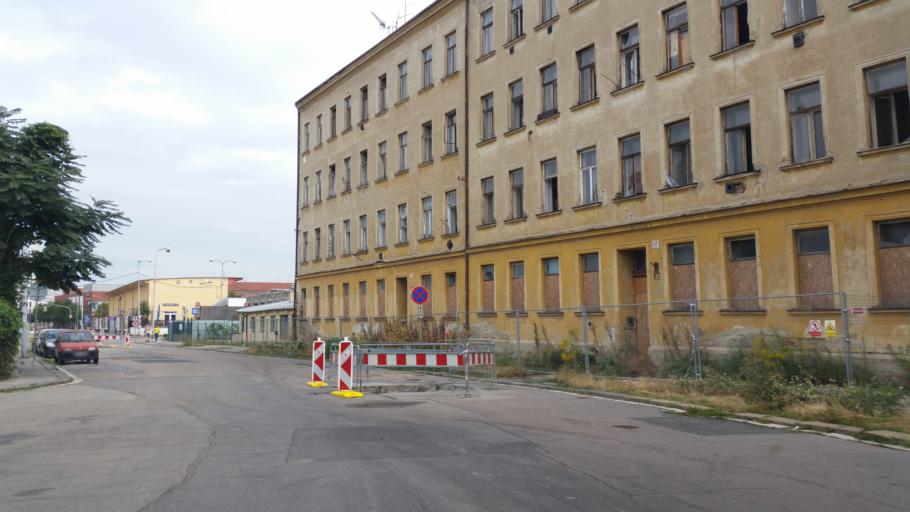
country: CZ
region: South Moravian
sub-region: Mesto Brno
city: Brno
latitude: 49.1841
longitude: 16.6161
